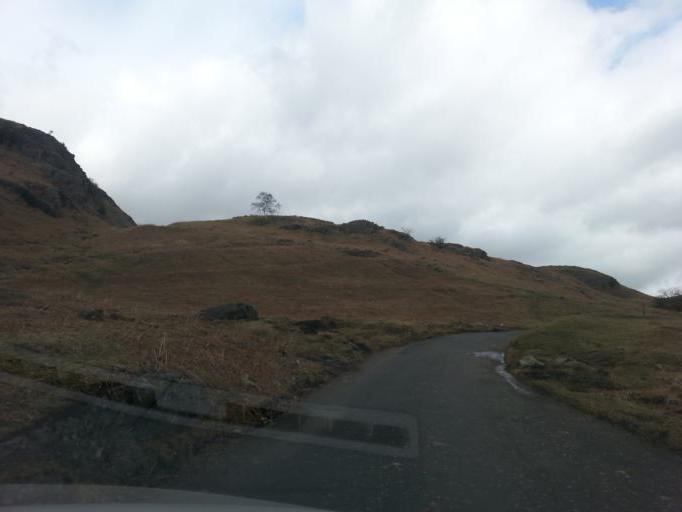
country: GB
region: England
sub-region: Cumbria
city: Ambleside
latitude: 54.4387
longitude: -3.0292
